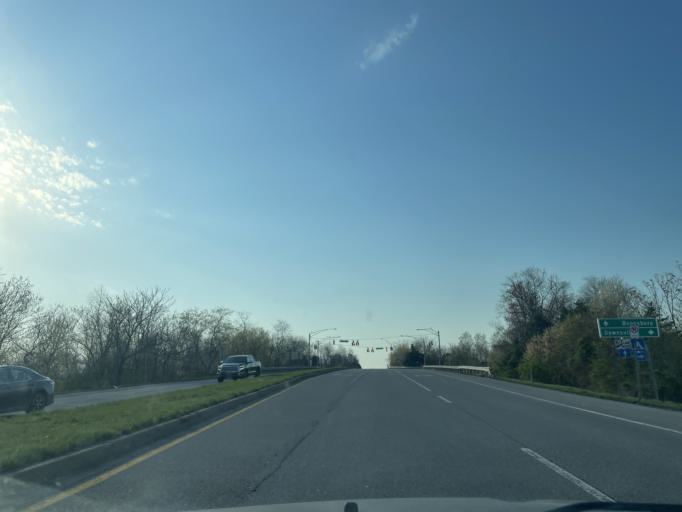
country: US
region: Maryland
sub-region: Washington County
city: Williamsport
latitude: 39.5860
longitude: -77.8145
